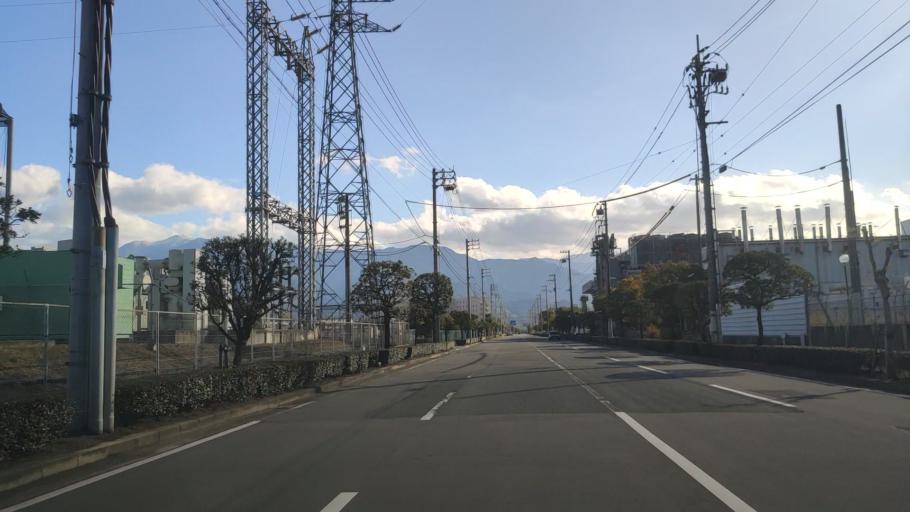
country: JP
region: Ehime
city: Saijo
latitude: 33.9391
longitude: 133.1916
